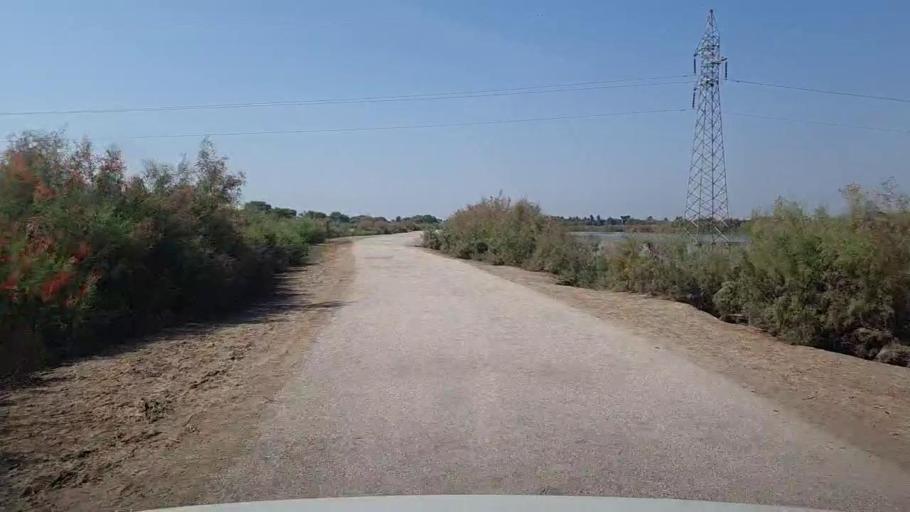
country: PK
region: Sindh
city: Kandhkot
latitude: 28.3350
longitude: 69.3656
